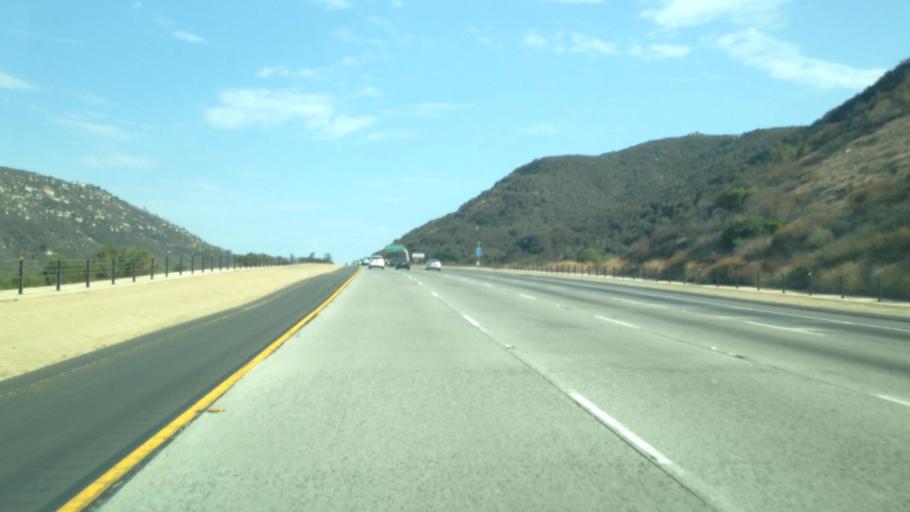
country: US
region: California
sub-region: San Diego County
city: Hidden Meadows
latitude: 33.2171
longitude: -117.1401
